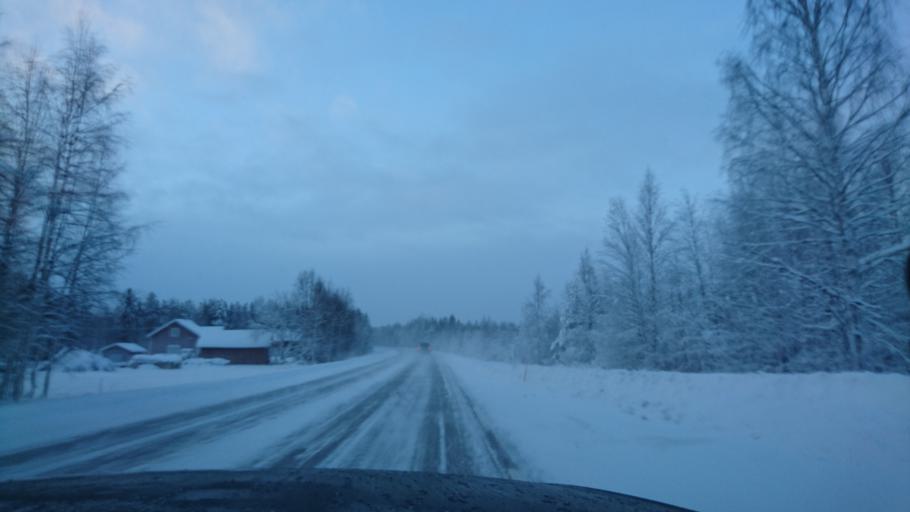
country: FI
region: Northern Ostrobothnia
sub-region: Koillismaa
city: Taivalkoski
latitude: 65.4668
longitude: 27.6618
